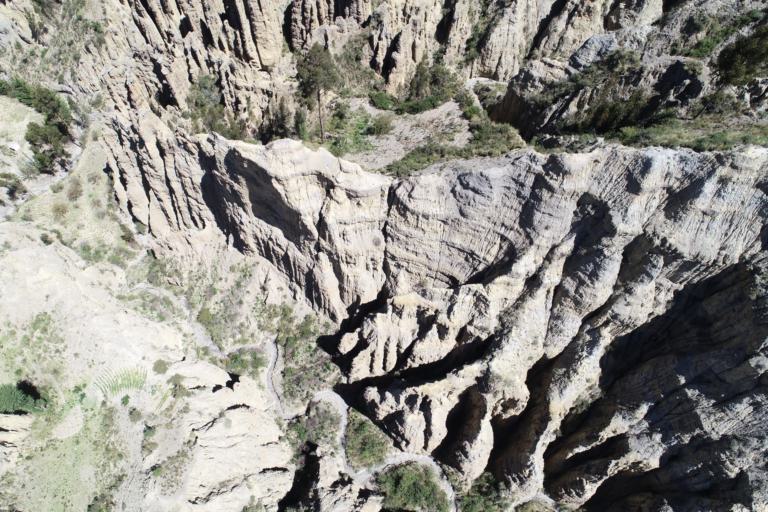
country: BO
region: La Paz
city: La Paz
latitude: -16.5036
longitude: -68.0651
